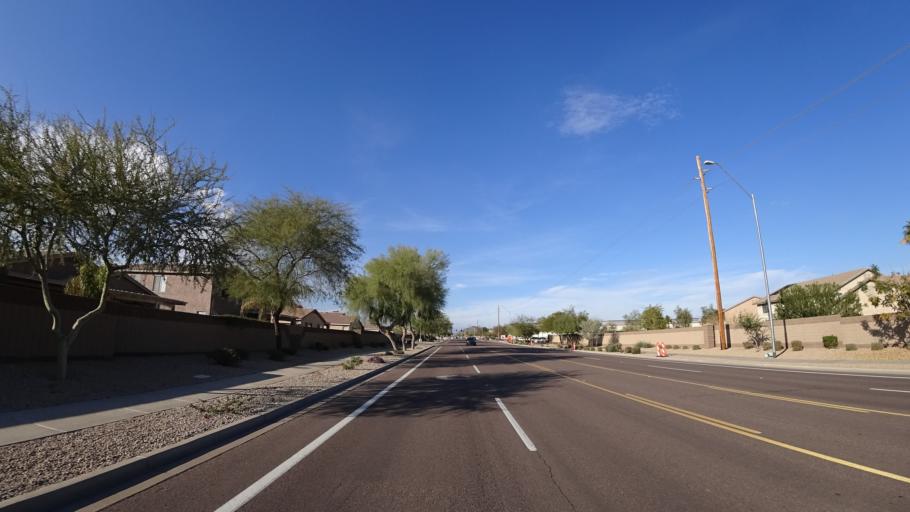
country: US
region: Arizona
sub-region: Maricopa County
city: Sun City
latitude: 33.6721
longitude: -112.2551
